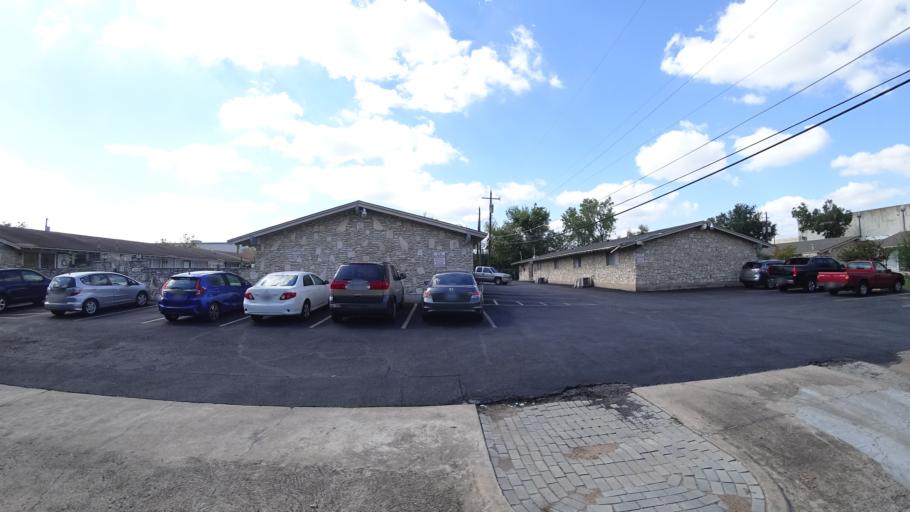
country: US
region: Texas
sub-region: Travis County
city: Austin
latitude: 30.3174
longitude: -97.7112
